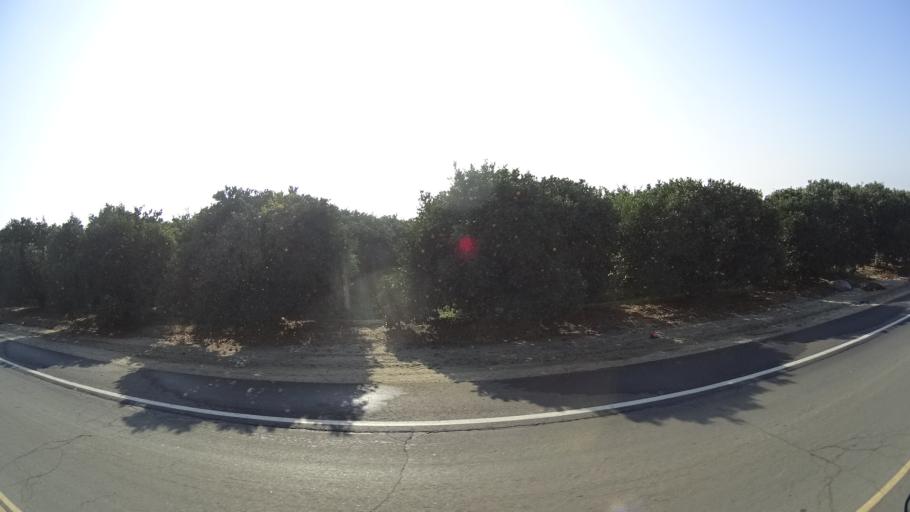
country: US
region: California
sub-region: Kern County
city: Lamont
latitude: 35.3618
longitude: -118.8814
